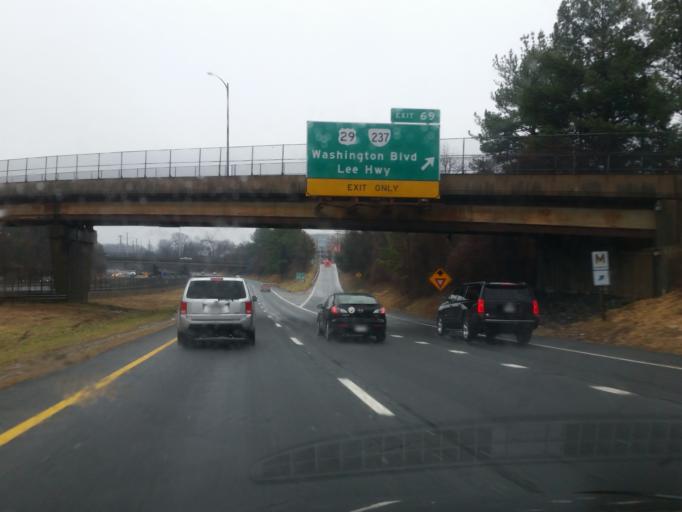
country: US
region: Virginia
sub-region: City of Falls Church
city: Falls Church
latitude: 38.8903
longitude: -77.1650
